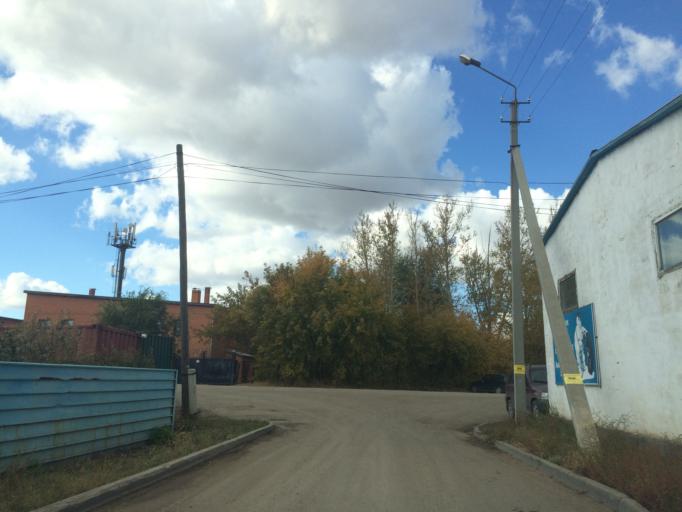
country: KZ
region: Astana Qalasy
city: Astana
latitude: 51.1861
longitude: 71.3671
